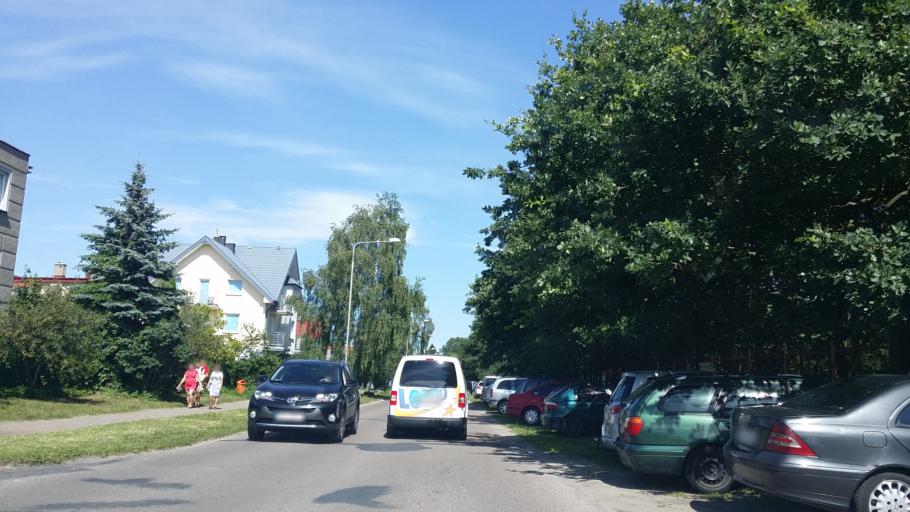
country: PL
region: West Pomeranian Voivodeship
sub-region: Powiat kolobrzeski
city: Kolobrzeg
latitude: 54.1726
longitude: 15.5377
